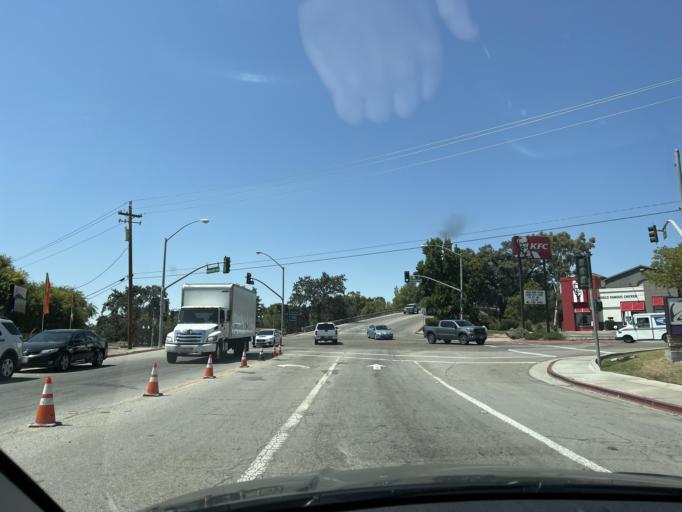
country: US
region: California
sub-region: San Luis Obispo County
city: Paso Robles
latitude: 35.6401
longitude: -120.6878
